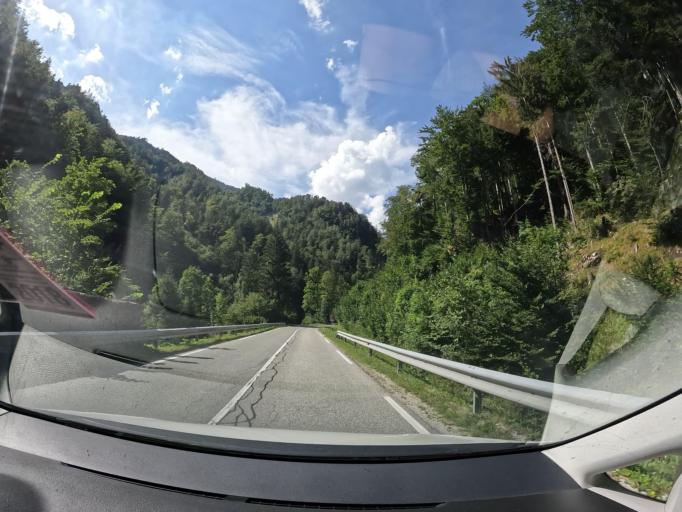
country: SI
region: Trzic
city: Trzic
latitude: 46.3927
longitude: 14.3495
